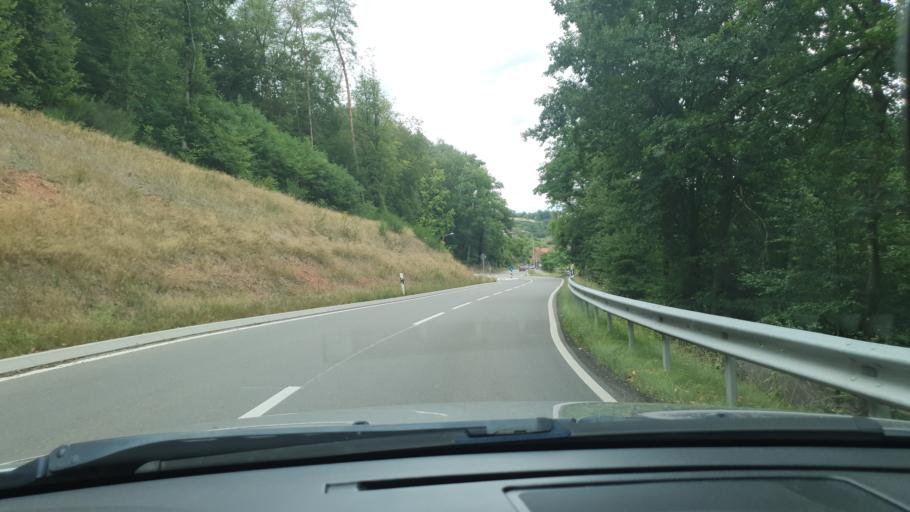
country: DE
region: Rheinland-Pfalz
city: Obernheim-Kirchenarnbach
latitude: 49.3489
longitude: 7.5715
